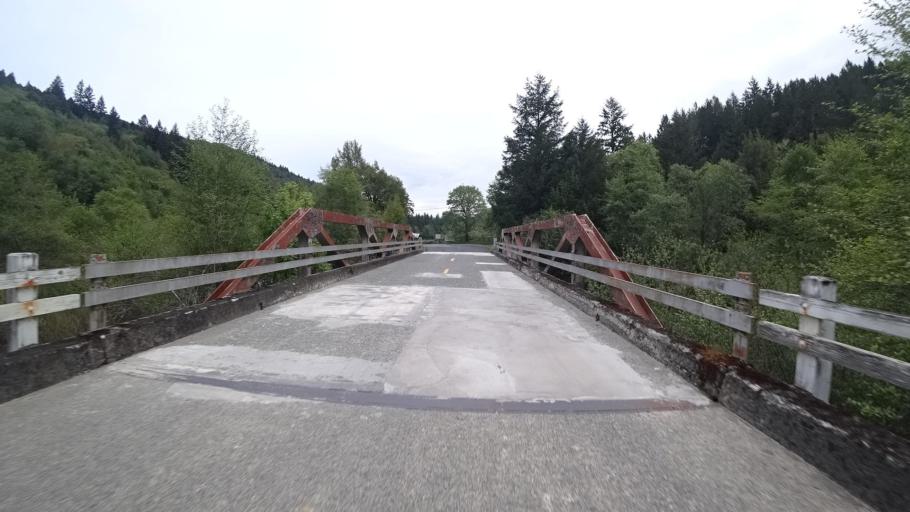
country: US
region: California
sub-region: Humboldt County
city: Blue Lake
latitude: 40.9636
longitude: -123.8405
